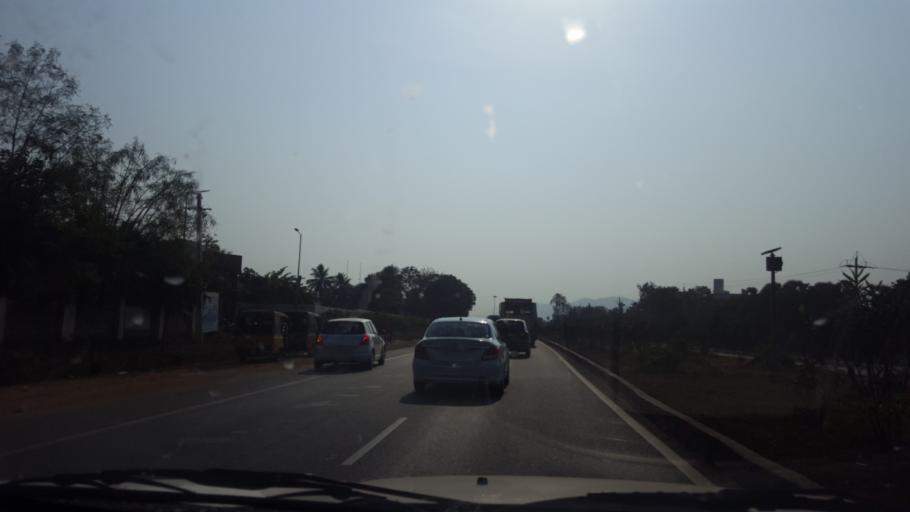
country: IN
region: Andhra Pradesh
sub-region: Vishakhapatnam
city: Anakapalle
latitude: 17.6547
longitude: 82.9284
